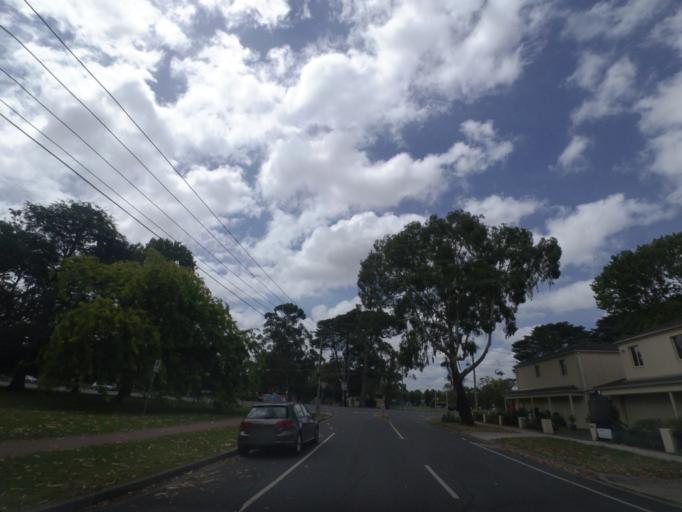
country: AU
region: Victoria
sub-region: Maroondah
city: Croydon South
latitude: -37.7997
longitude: 145.2852
